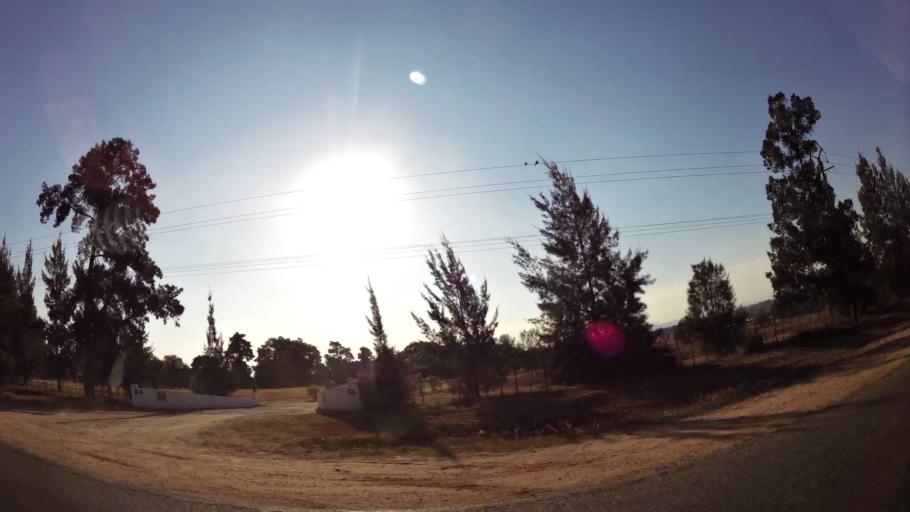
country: ZA
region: Gauteng
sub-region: West Rand District Municipality
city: Muldersdriseloop
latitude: -26.0181
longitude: 27.8832
